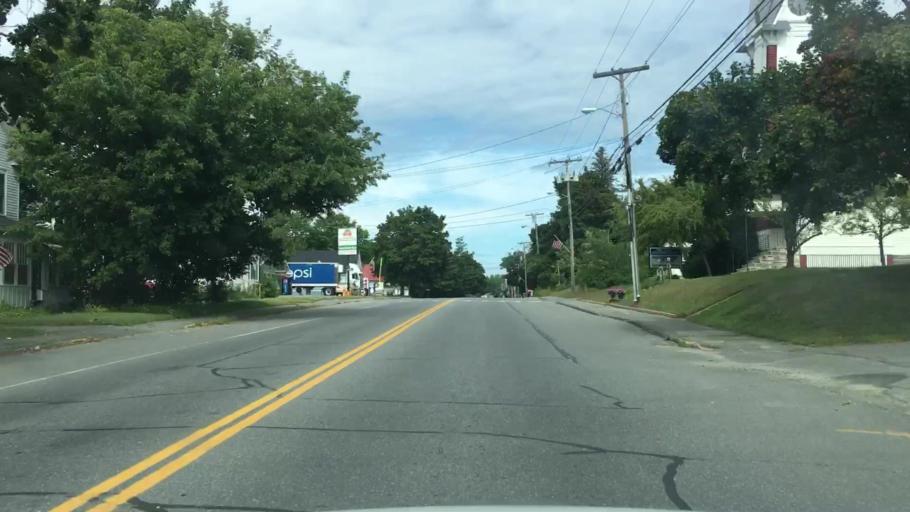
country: US
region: Maine
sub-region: Piscataquis County
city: Milo
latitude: 45.2539
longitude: -68.9864
